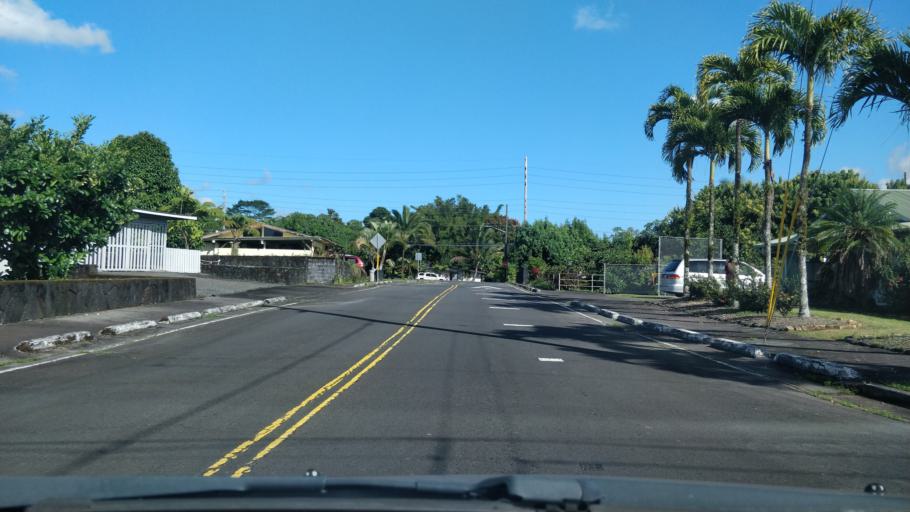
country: US
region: Hawaii
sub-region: Hawaii County
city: Hilo
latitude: 19.6823
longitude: -155.0868
